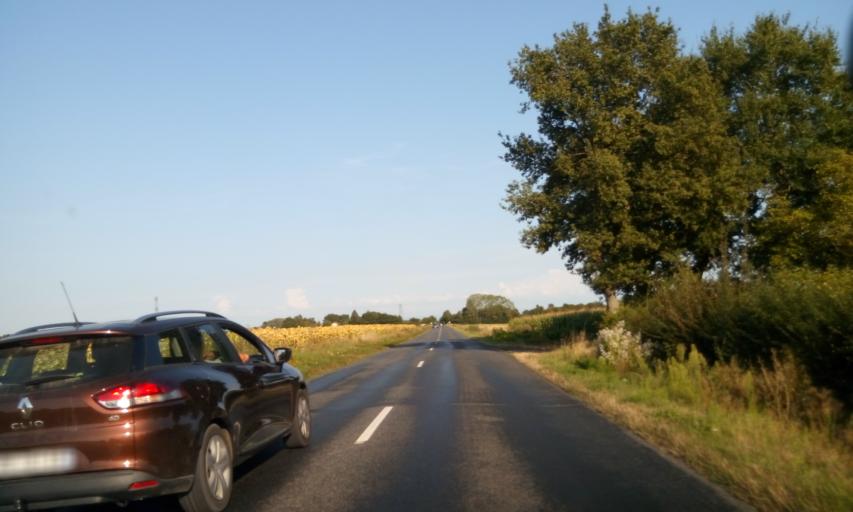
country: FR
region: Rhone-Alpes
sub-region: Departement de l'Ain
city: Amberieux-en-Dombes
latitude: 45.9982
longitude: 4.9134
